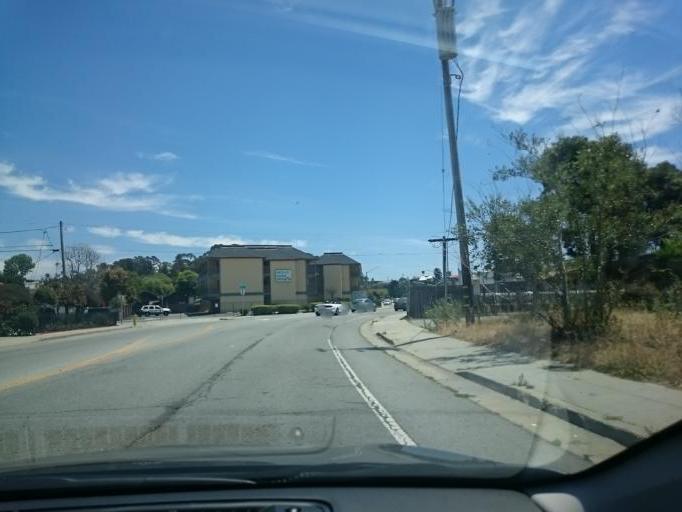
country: US
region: California
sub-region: Santa Cruz County
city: Santa Cruz
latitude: 36.9690
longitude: -122.0180
